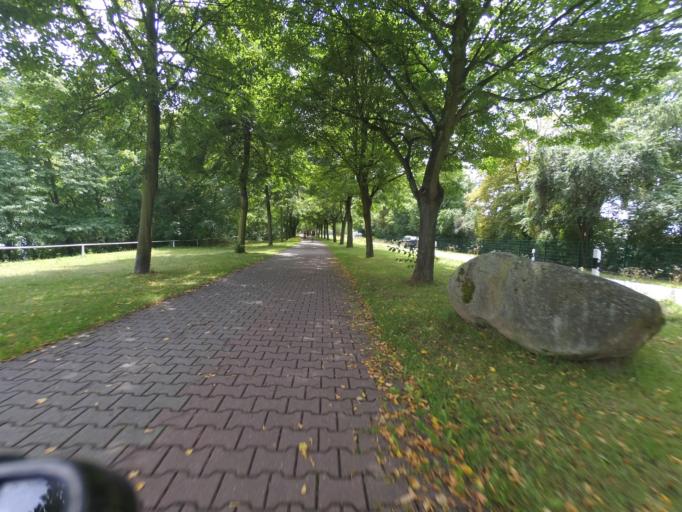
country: DE
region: Saxony
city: Heidenau
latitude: 50.9752
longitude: 13.8890
